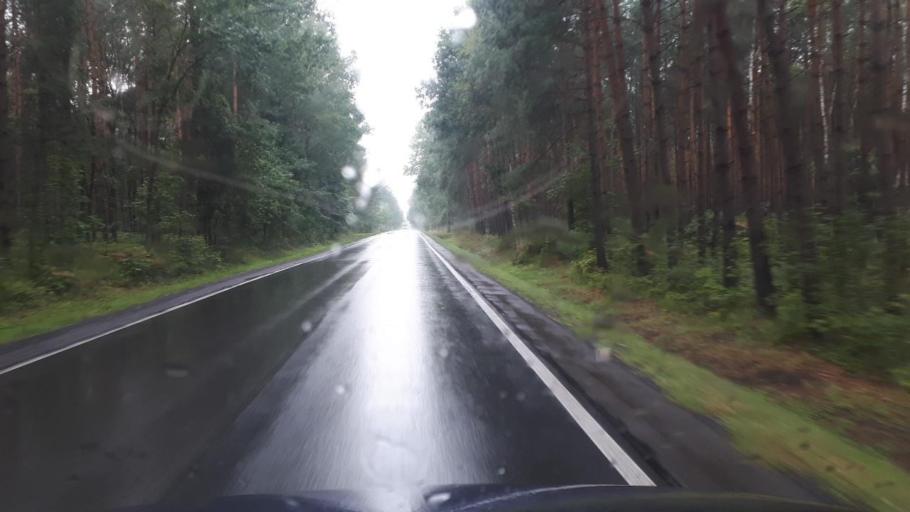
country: PL
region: Silesian Voivodeship
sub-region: Powiat tarnogorski
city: Tworog
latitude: 50.5303
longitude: 18.6889
